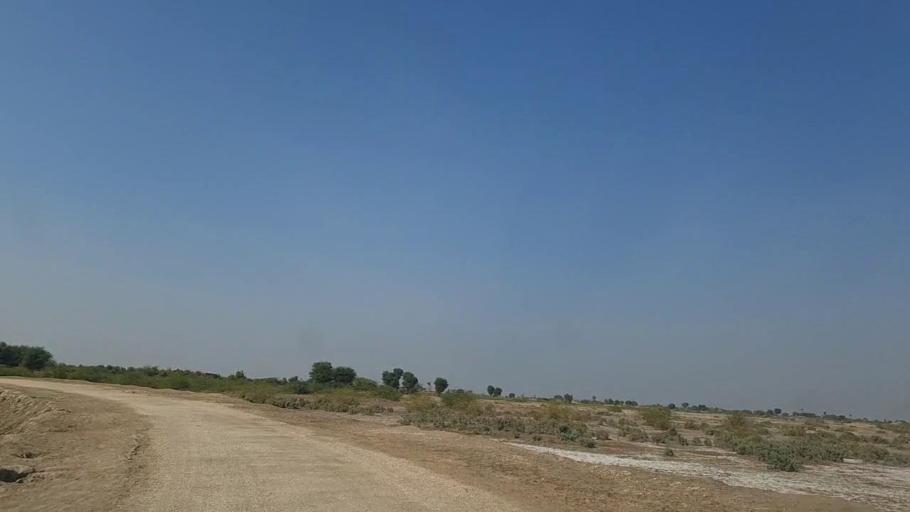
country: PK
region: Sindh
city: Naukot
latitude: 24.9011
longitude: 69.4470
